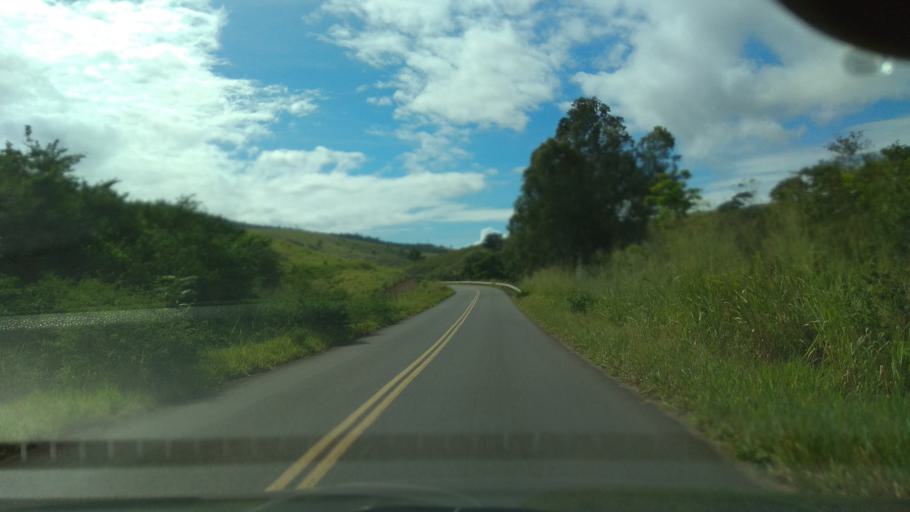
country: BR
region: Bahia
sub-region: Ubaira
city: Ubaira
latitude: -13.2627
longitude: -39.7074
